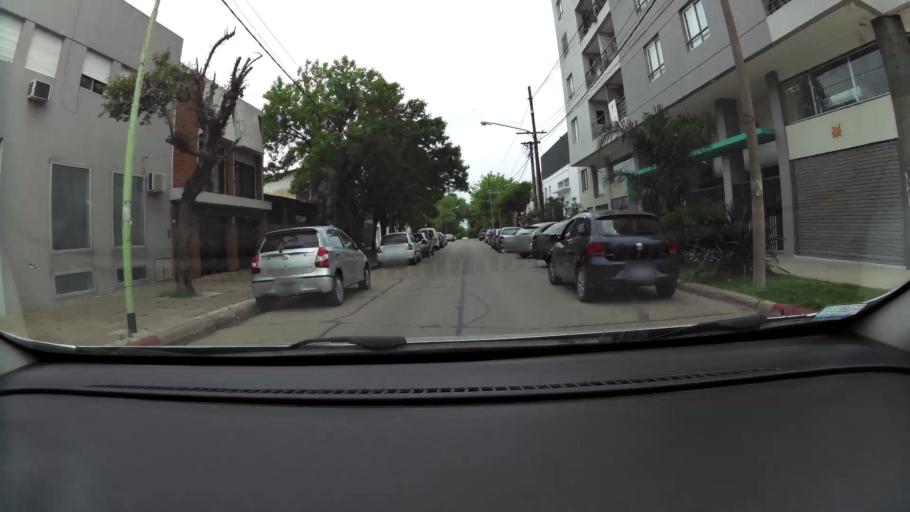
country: AR
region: Buenos Aires
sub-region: Partido de Campana
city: Campana
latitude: -34.1640
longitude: -58.9639
